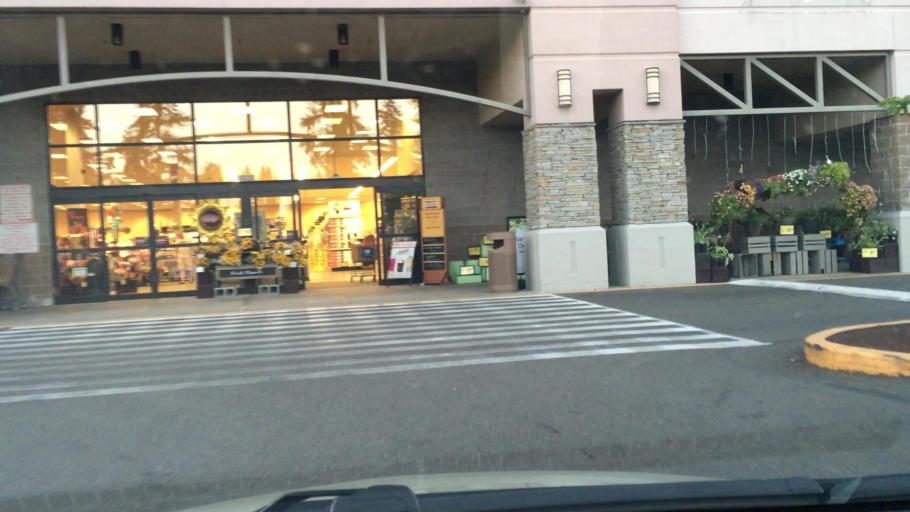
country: US
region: Washington
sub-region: King County
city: Inglewood-Finn Hill
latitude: 47.7232
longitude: -122.2067
